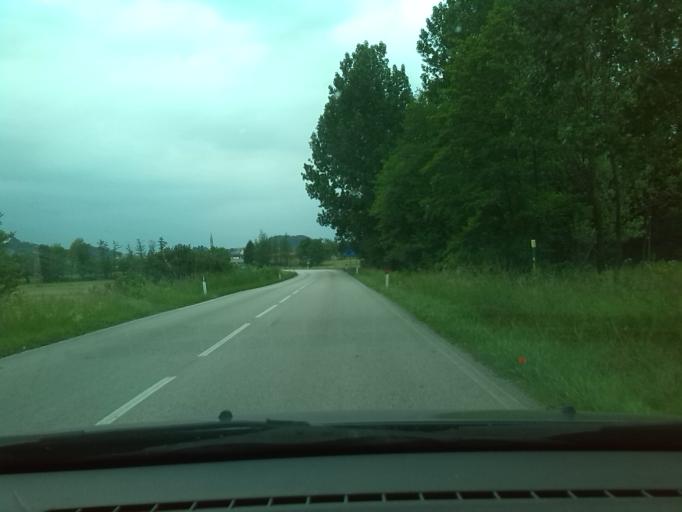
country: IT
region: Friuli Venezia Giulia
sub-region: Provincia di Udine
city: Treppo Grande
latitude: 46.2137
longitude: 13.1513
